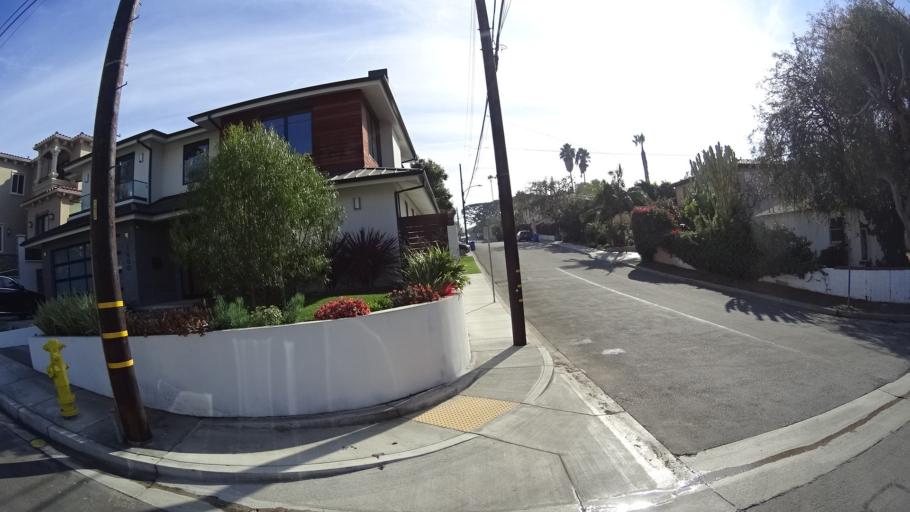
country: US
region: California
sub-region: Los Angeles County
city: Hermosa Beach
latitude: 33.8794
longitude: -118.3851
